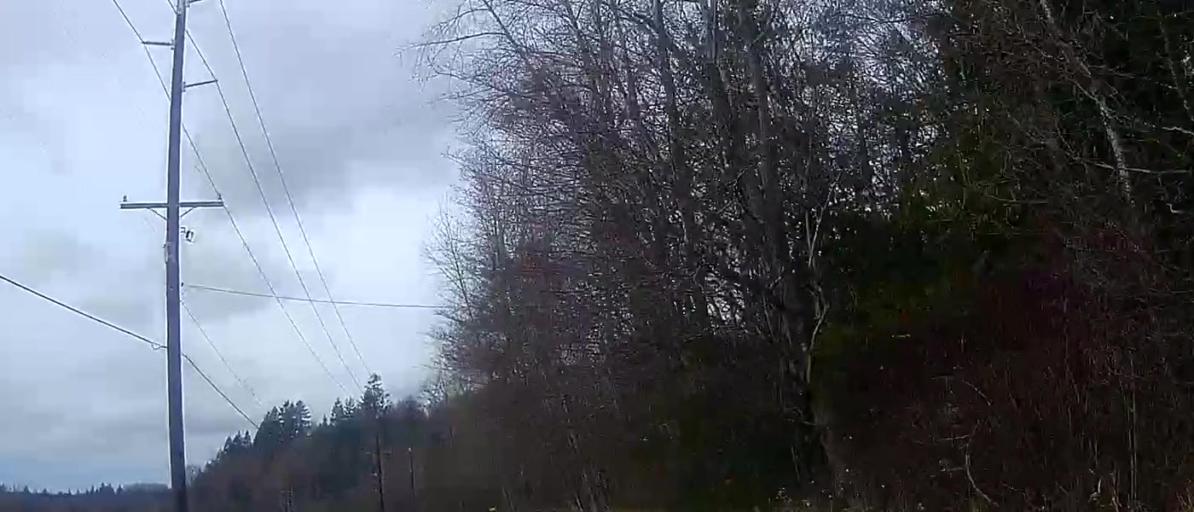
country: US
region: Washington
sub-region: Skagit County
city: Burlington
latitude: 48.5596
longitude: -122.3188
